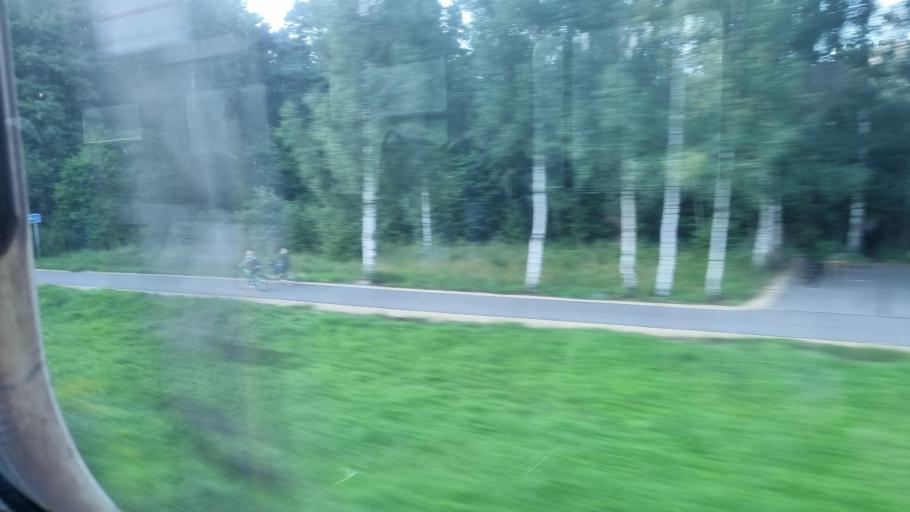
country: LV
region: Babite
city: Pinki
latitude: 56.9646
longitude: 23.9187
